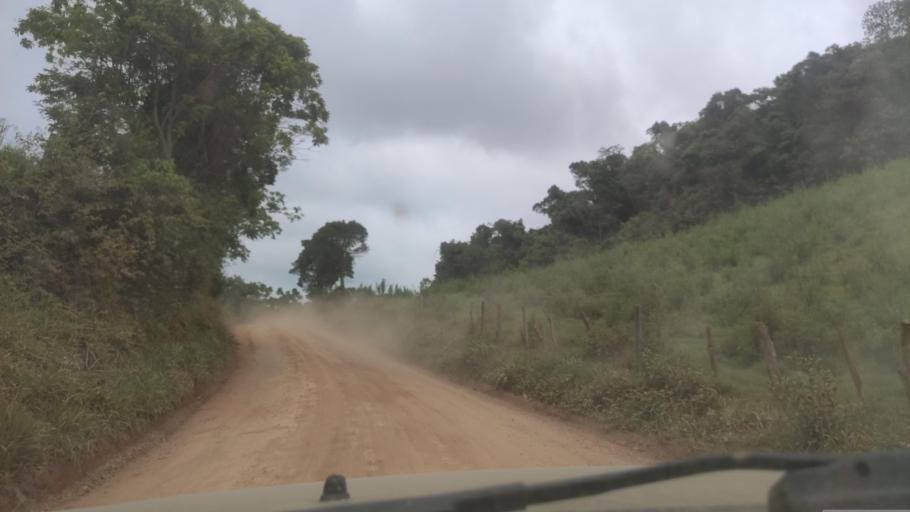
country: BR
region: Minas Gerais
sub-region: Paraisopolis
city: Paraisopolis
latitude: -22.6595
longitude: -45.9020
